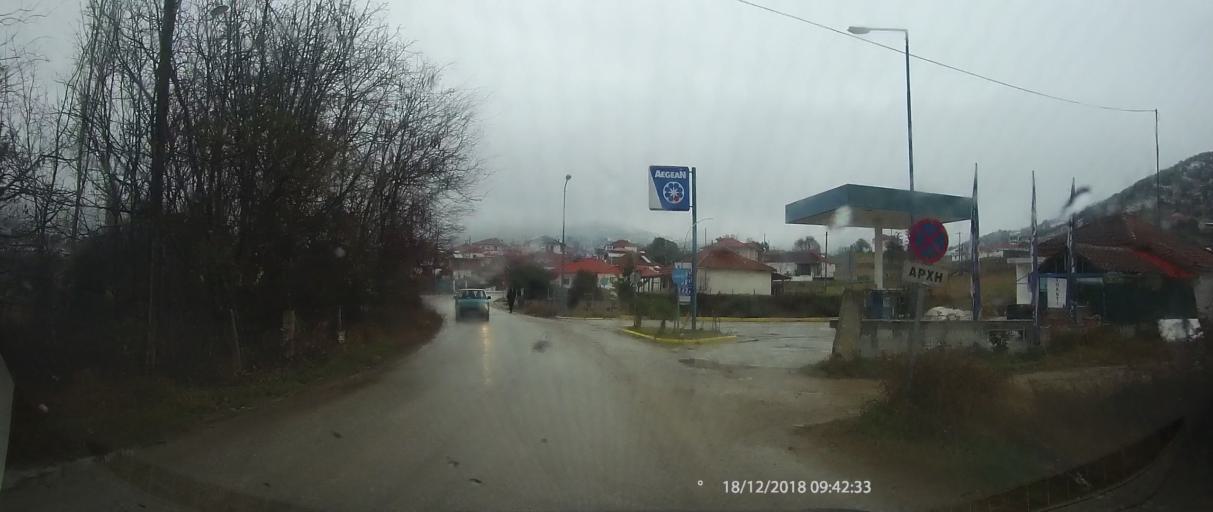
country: GR
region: Thessaly
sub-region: Nomos Larisis
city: Livadi
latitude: 40.0206
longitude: 22.2380
